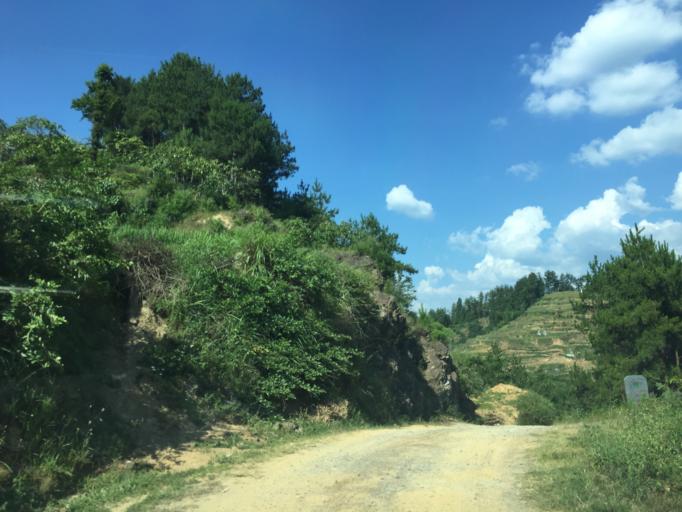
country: CN
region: Guizhou Sheng
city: Tongjing
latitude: 28.3306
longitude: 108.2976
